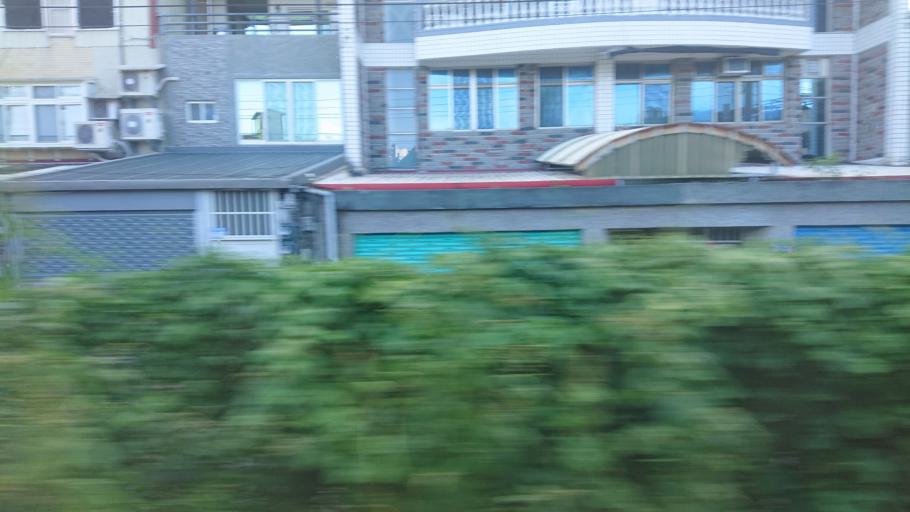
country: TW
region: Taiwan
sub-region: Hualien
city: Hualian
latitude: 23.9757
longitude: 121.5925
